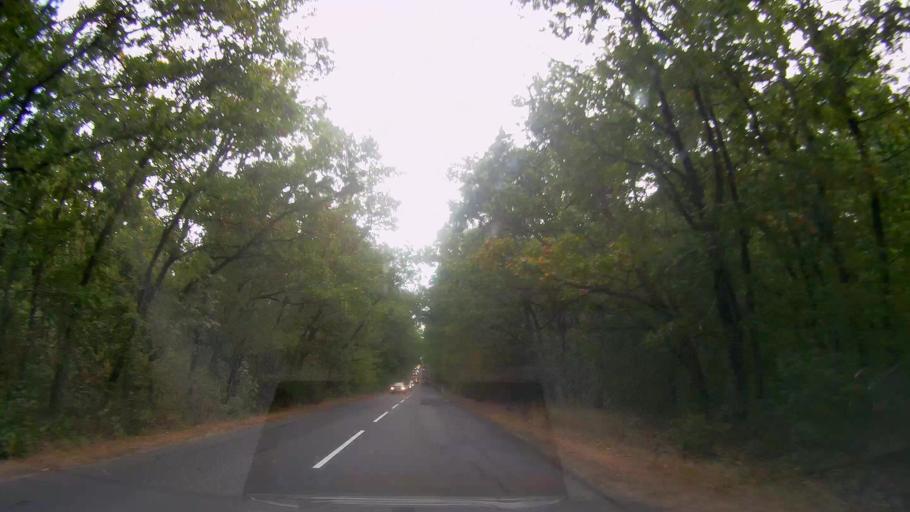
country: BG
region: Burgas
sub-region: Obshtina Primorsko
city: Primorsko
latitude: 42.2820
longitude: 27.7379
